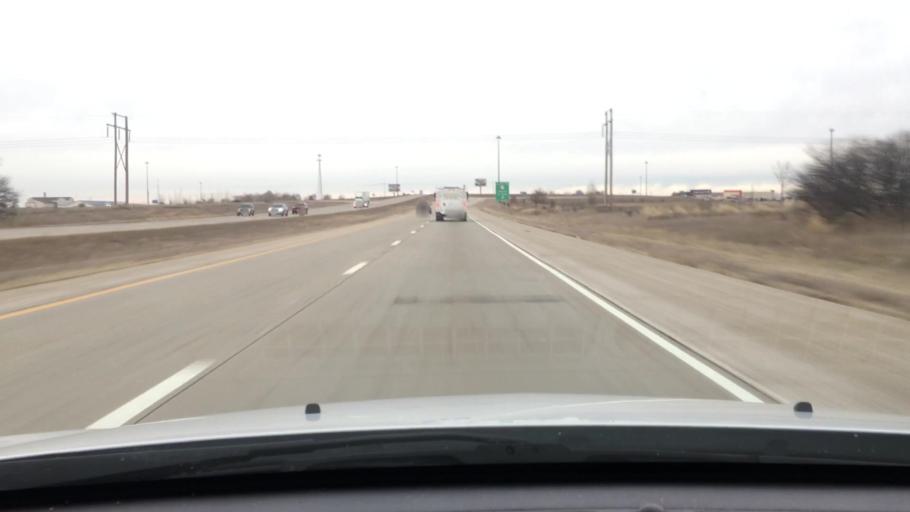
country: US
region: Illinois
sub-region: Woodford County
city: El Paso
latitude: 40.7286
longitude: -89.0341
